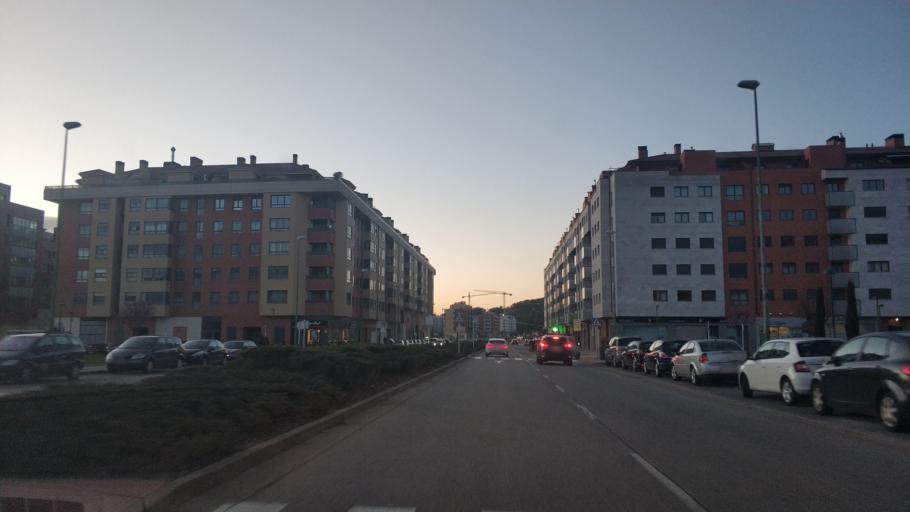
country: ES
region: Castille and Leon
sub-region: Provincia de Burgos
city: Burgos
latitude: 42.3598
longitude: -3.6664
